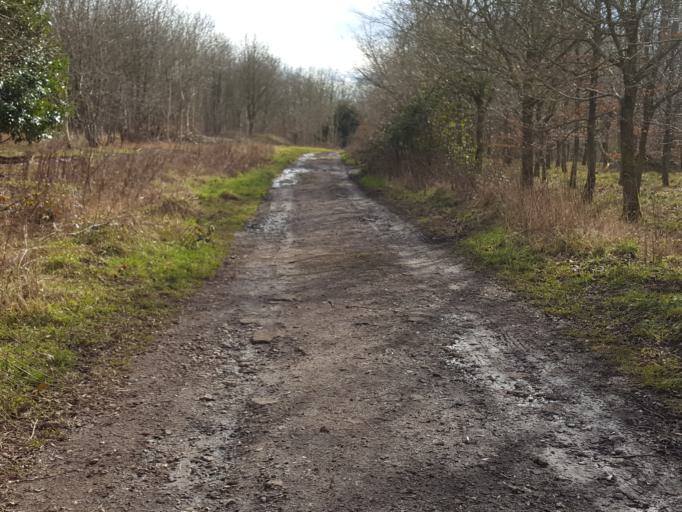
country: GB
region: England
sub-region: Buckinghamshire
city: High Wycombe
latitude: 51.6535
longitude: -0.8110
